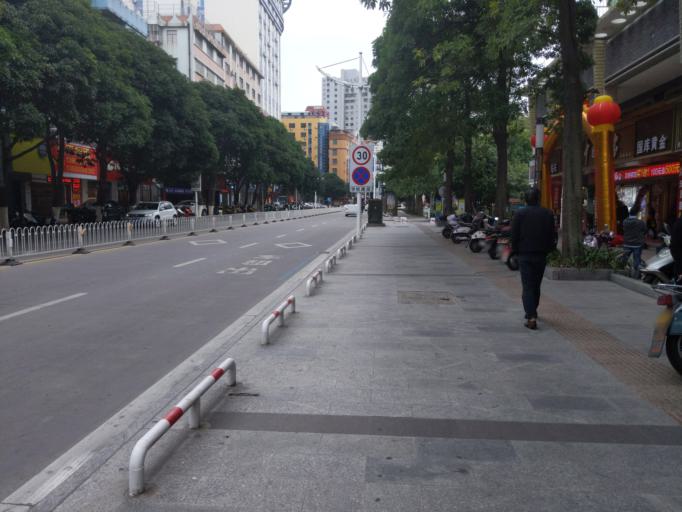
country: CN
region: Fujian
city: Shishi
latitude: 24.7353
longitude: 118.6275
